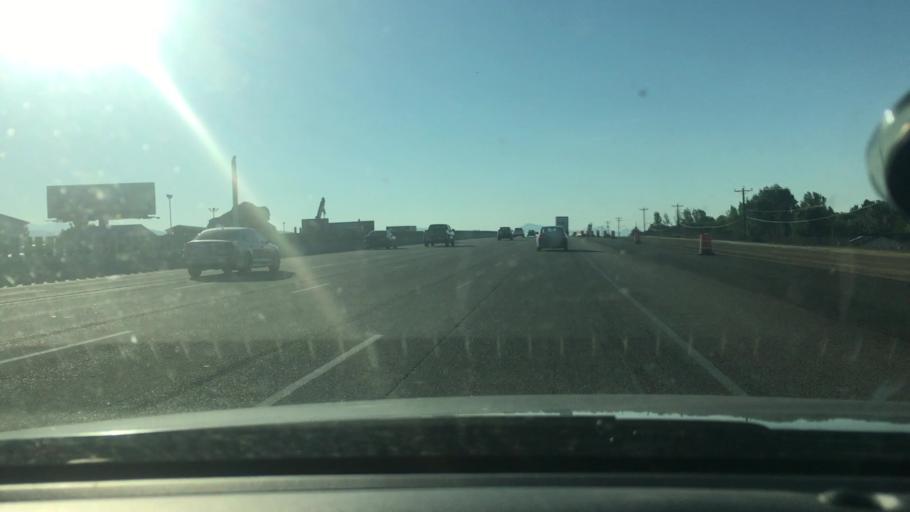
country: US
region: Utah
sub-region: Utah County
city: Lehi
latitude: 40.4029
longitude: -111.8520
